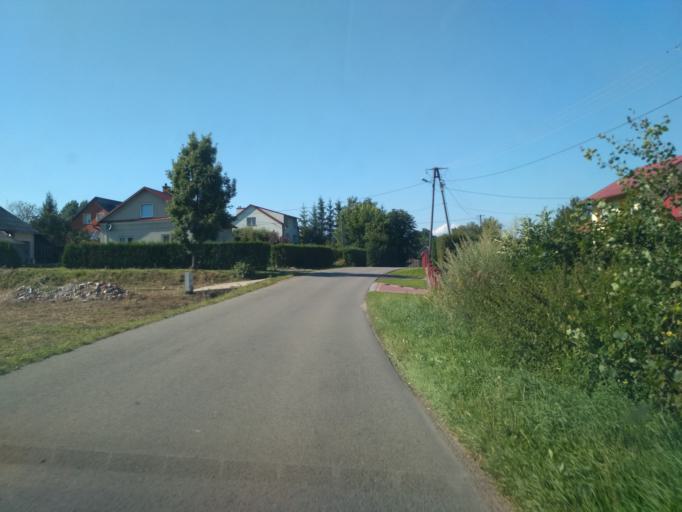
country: PL
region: Subcarpathian Voivodeship
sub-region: Powiat strzyzowski
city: Wysoka Strzyzowska
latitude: 49.8254
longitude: 21.7390
